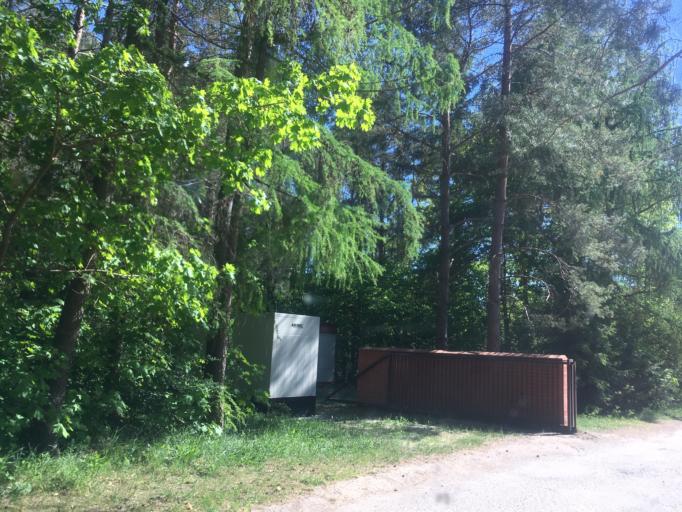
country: PL
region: Warmian-Masurian Voivodeship
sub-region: Powiat mragowski
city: Mikolajki
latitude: 53.7552
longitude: 21.6095
